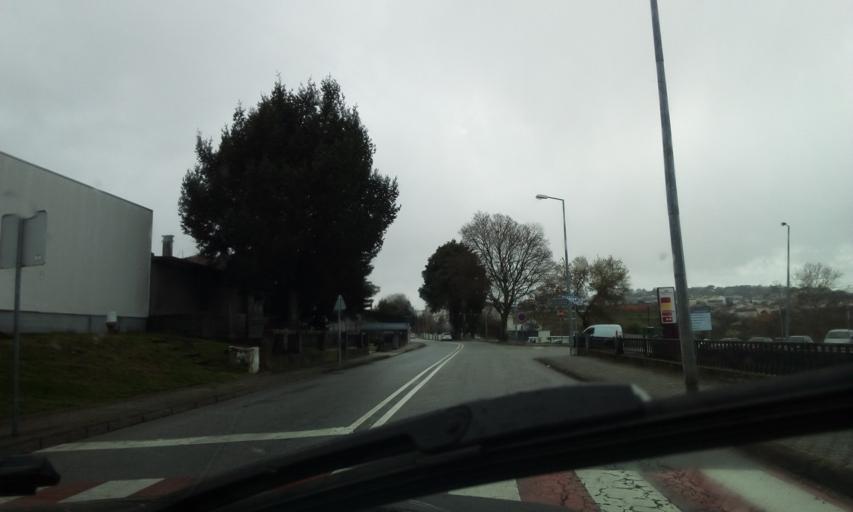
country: PT
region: Viseu
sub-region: Mangualde
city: Mangualde
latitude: 40.6153
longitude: -7.7594
